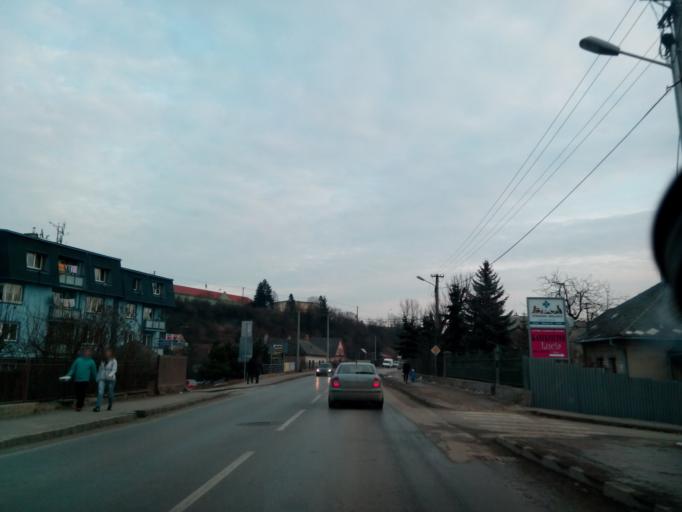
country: SK
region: Presovsky
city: Sabinov
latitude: 49.1001
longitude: 21.1044
